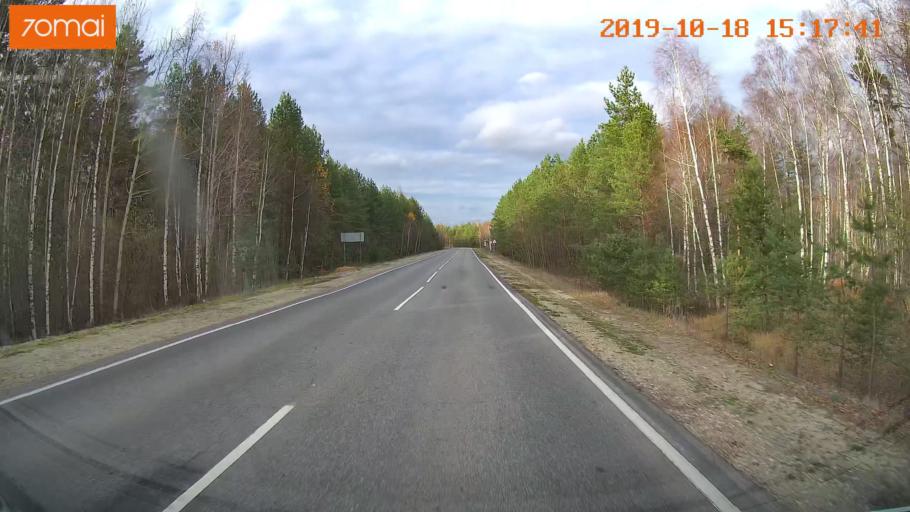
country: RU
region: Vladimir
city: Anopino
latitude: 55.6535
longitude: 40.7270
